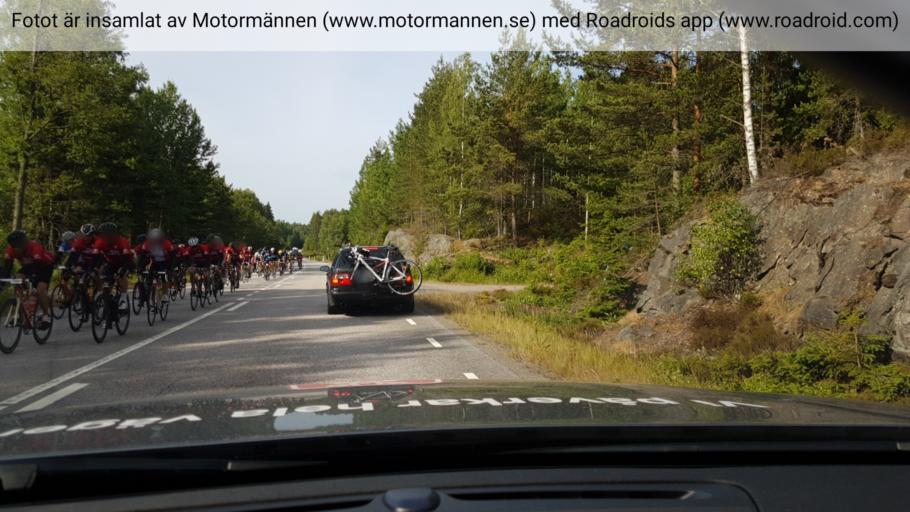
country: SE
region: Vaestra Goetaland
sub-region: Karlsborgs Kommun
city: Karlsborg
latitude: 58.6494
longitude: 14.5717
